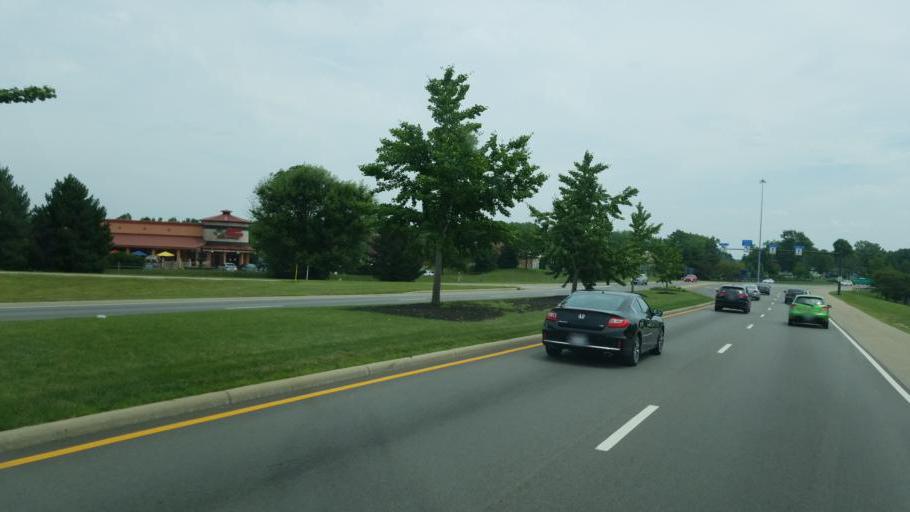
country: US
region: Ohio
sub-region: Franklin County
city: Hilliard
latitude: 40.0334
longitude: -83.1209
